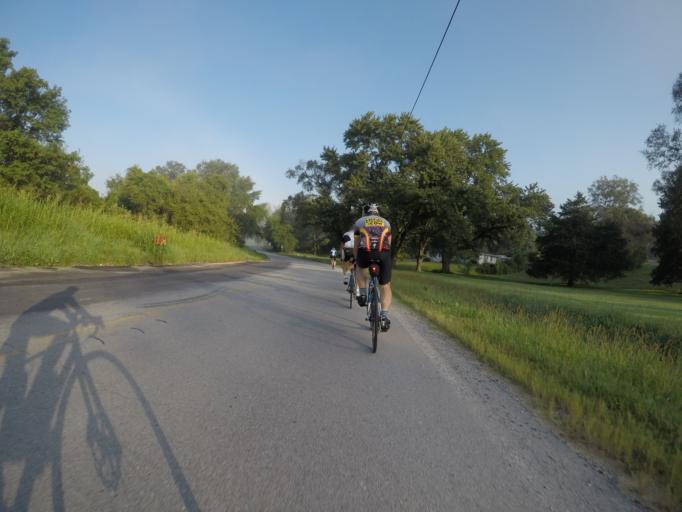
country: US
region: Kansas
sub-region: Leavenworth County
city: Lansing
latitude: 39.2629
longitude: -94.8822
